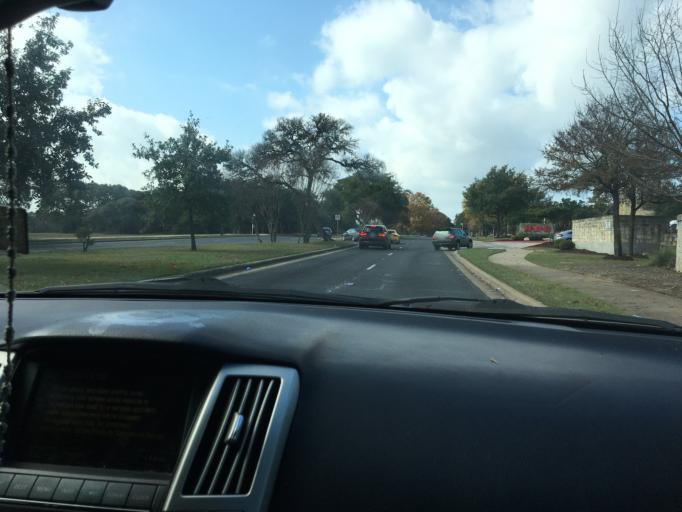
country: US
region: Texas
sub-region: Travis County
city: Shady Hollow
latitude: 30.2005
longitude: -97.8751
